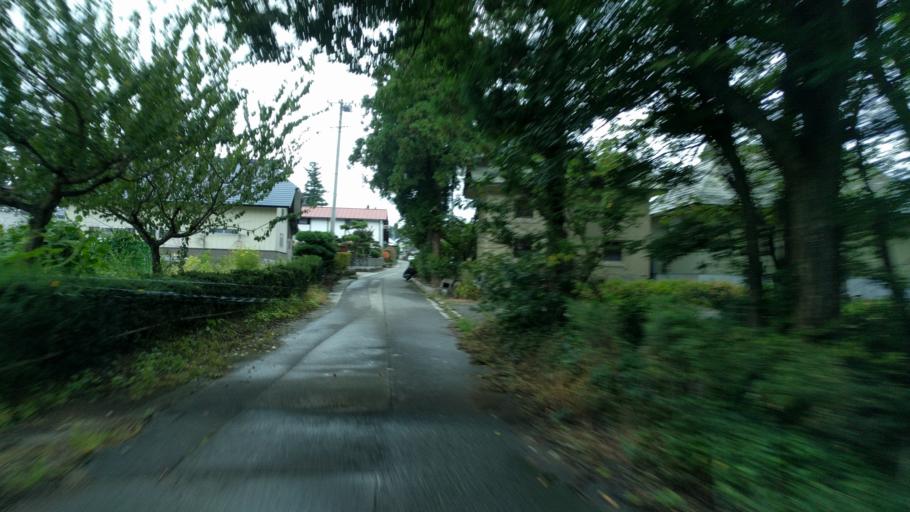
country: JP
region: Fukushima
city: Kitakata
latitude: 37.6172
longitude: 139.8315
